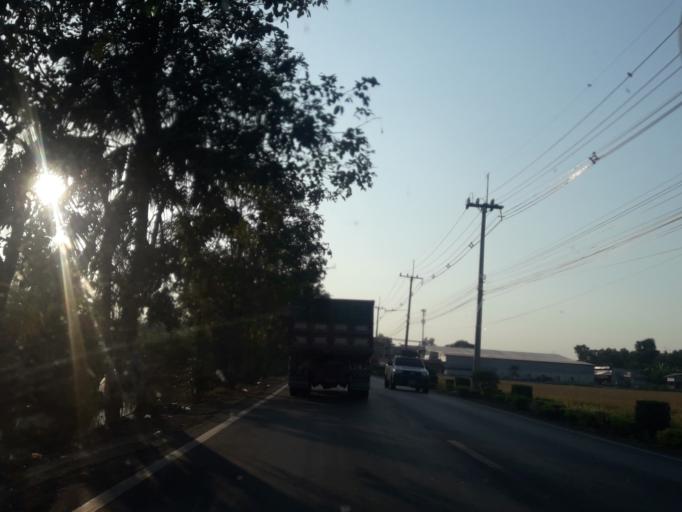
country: TH
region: Pathum Thani
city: Nong Suea
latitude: 14.1372
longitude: 100.8280
